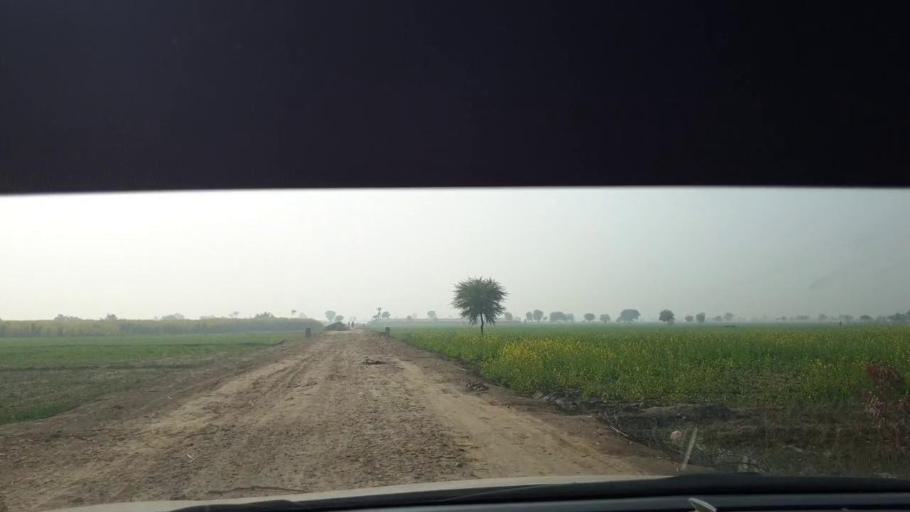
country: PK
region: Sindh
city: Berani
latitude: 25.7843
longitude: 68.7977
